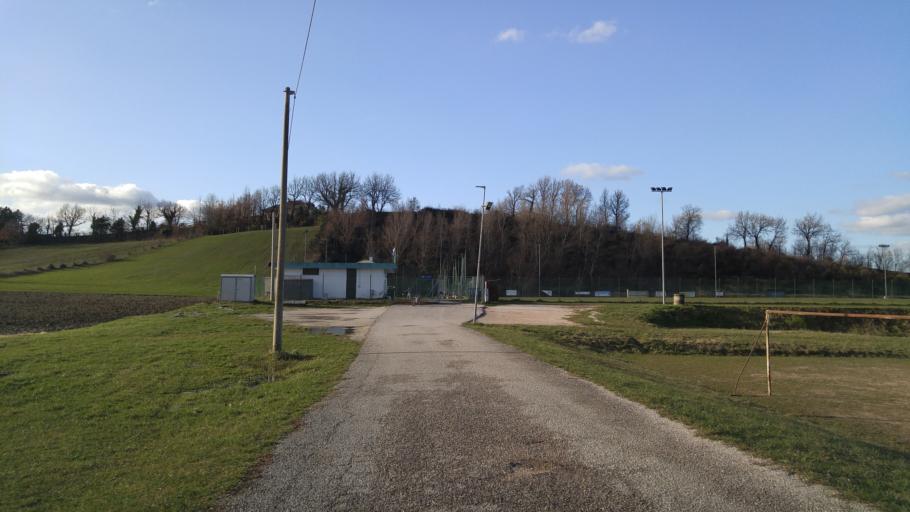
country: IT
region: The Marches
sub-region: Provincia di Pesaro e Urbino
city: Cagli
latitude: 43.5325
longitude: 12.6908
